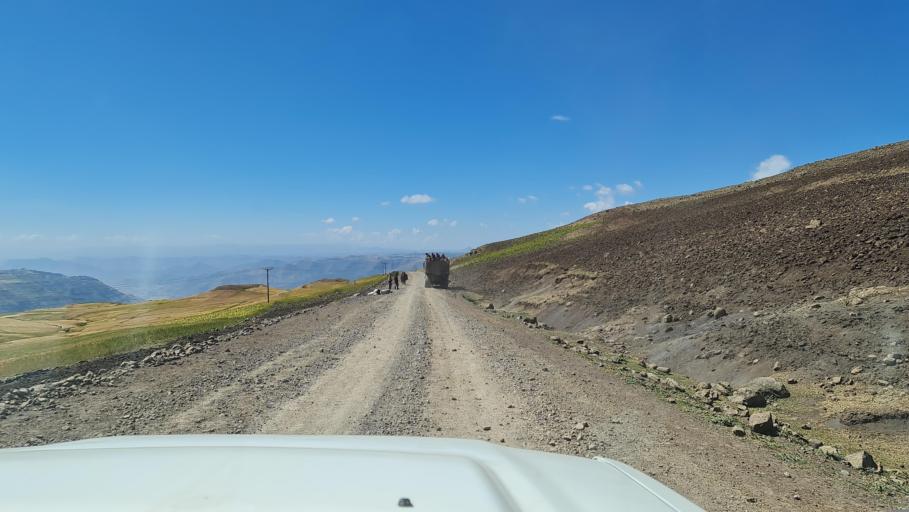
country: ET
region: Amhara
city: Debark'
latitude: 13.2363
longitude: 38.1093
